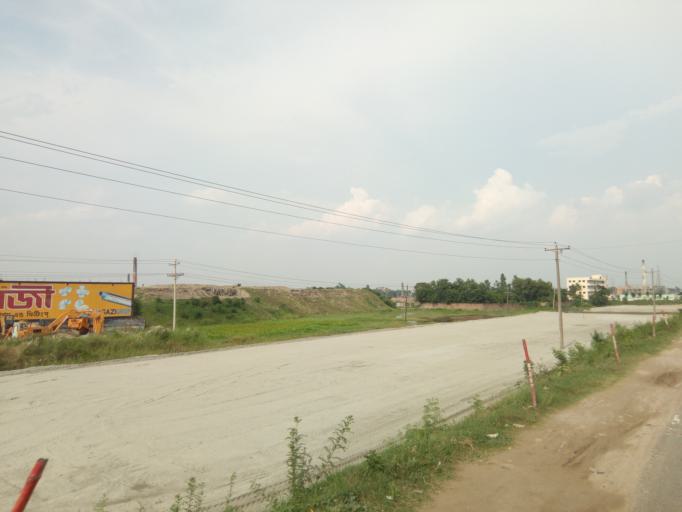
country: BD
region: Dhaka
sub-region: Dhaka
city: Dhaka
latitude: 23.6620
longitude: 90.3780
